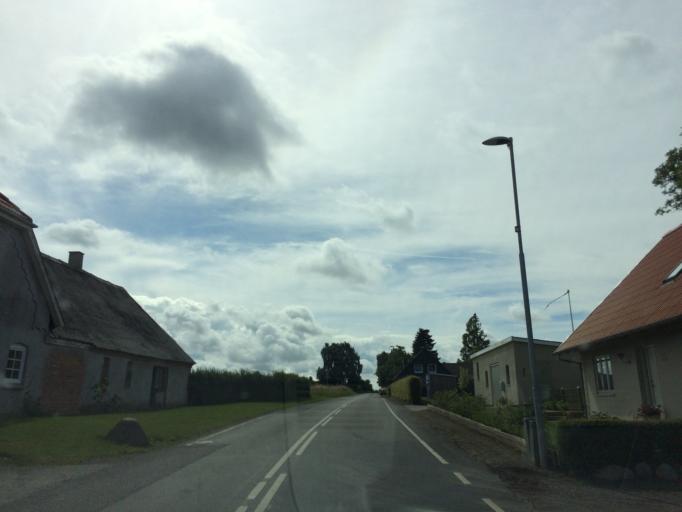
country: DK
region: South Denmark
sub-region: Odense Kommune
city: Bellinge
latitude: 55.2759
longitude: 10.3075
